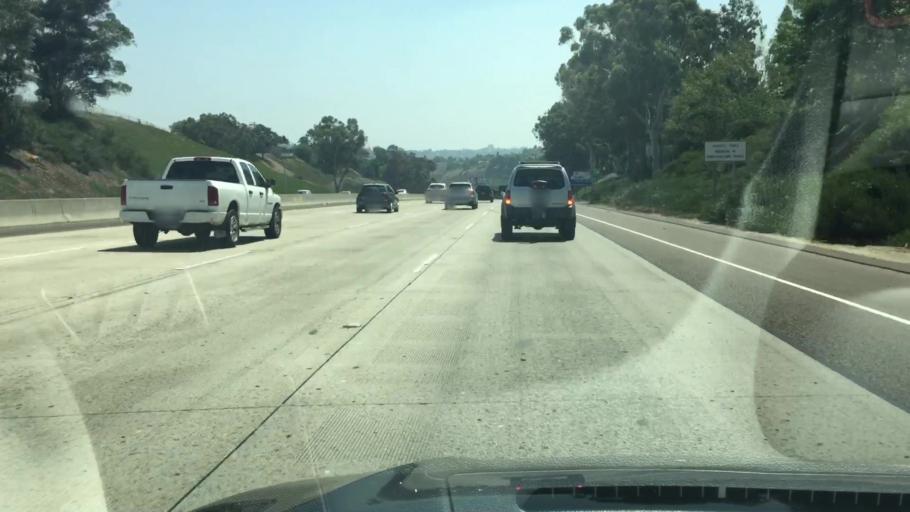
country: US
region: California
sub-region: San Diego County
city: San Diego
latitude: 32.7869
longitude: -117.1610
